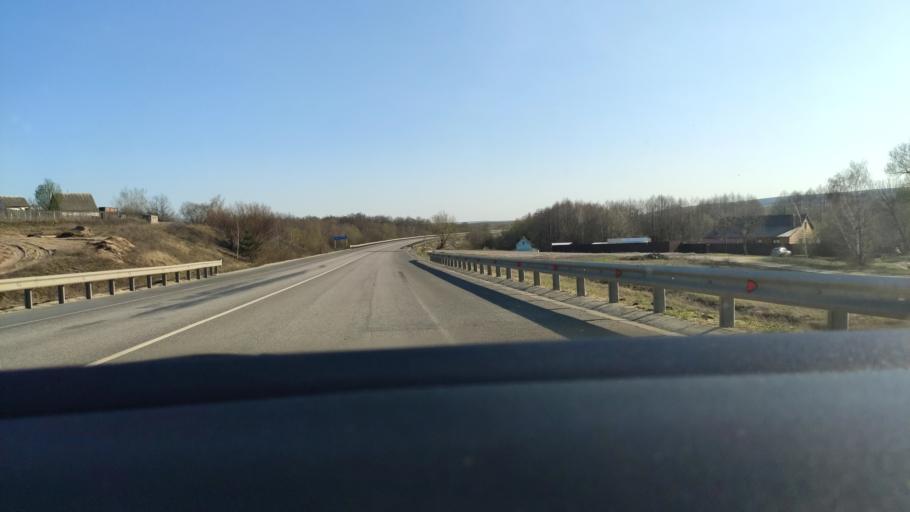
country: RU
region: Voronezj
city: Kolodeznyy
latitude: 51.3483
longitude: 39.1731
